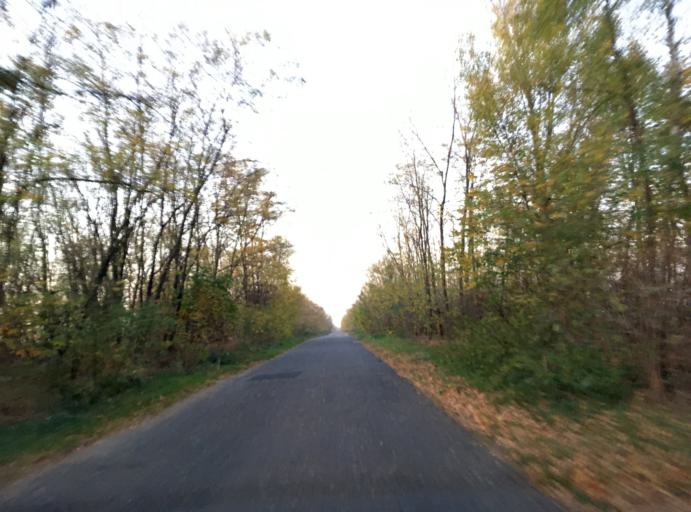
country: HU
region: Komarom-Esztergom
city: Acs
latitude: 47.7192
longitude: 18.0212
